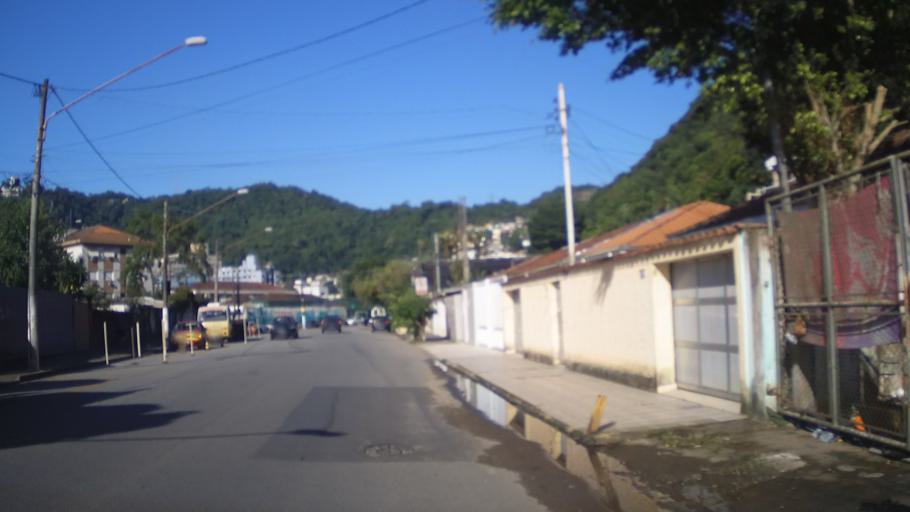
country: BR
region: Sao Paulo
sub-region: Santos
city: Santos
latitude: -23.9505
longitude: -46.3466
